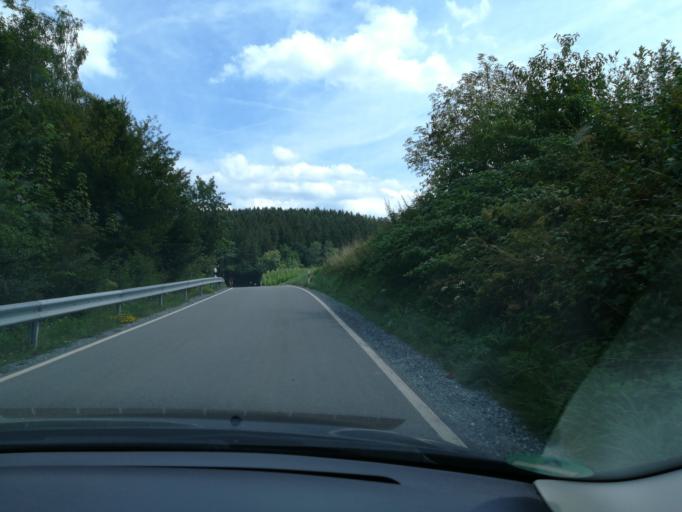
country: DE
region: Bavaria
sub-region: Upper Bavaria
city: Bruck
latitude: 48.0330
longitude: 11.8972
